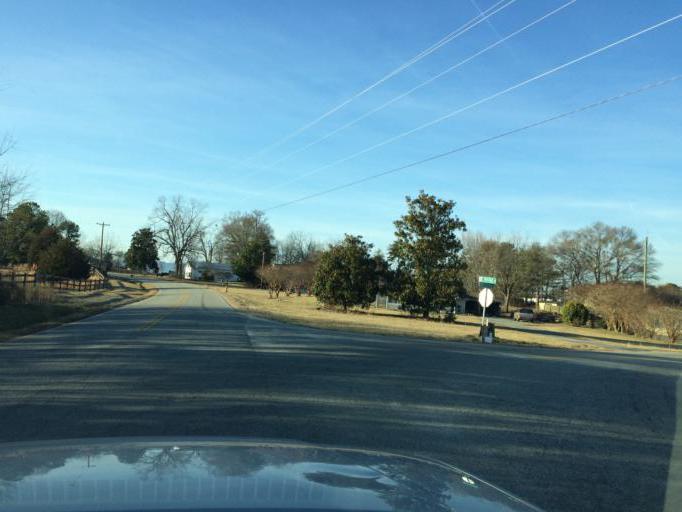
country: US
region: South Carolina
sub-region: Spartanburg County
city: Landrum
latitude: 35.1450
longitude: -82.1035
